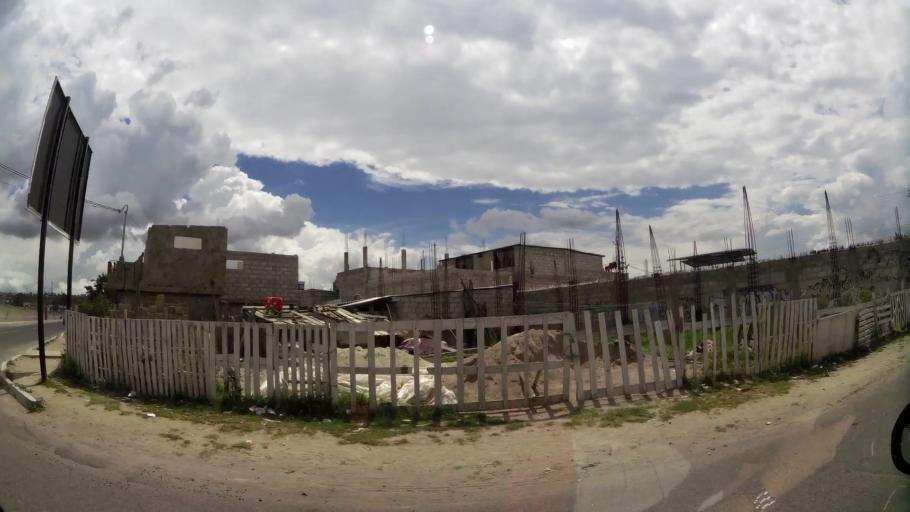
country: EC
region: Pichincha
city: Quito
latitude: -0.0817
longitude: -78.4147
